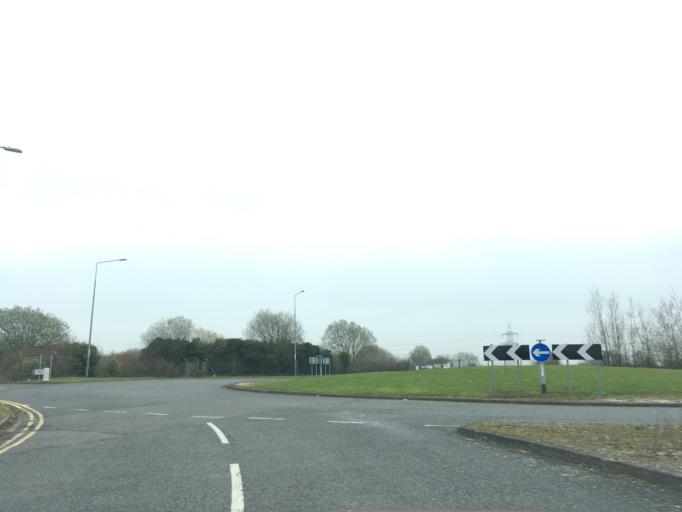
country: GB
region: Wales
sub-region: Newport
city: Marshfield
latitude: 51.5520
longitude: -3.0356
